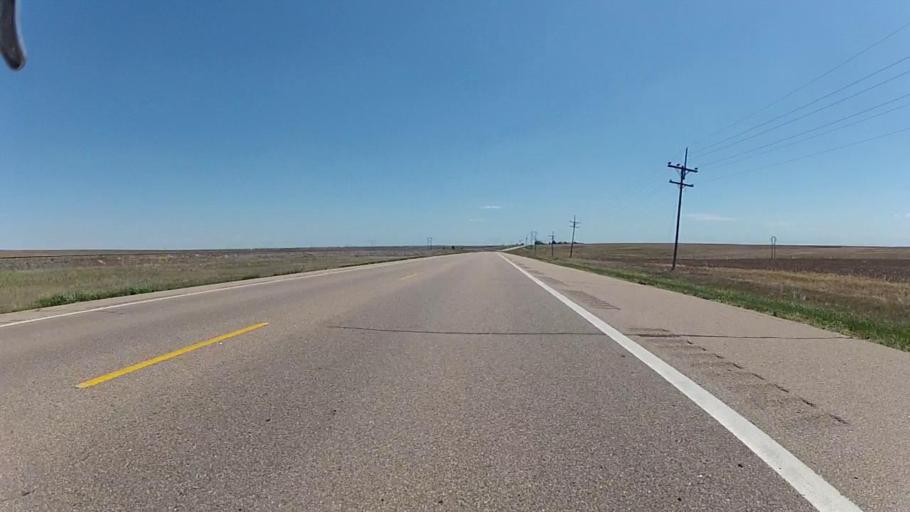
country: US
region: Kansas
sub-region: Ford County
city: Dodge City
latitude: 37.7037
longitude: -100.1414
